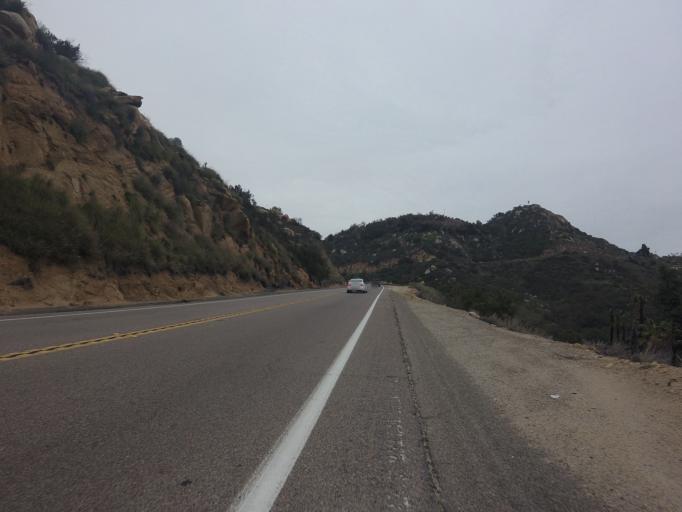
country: US
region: California
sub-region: San Diego County
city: Hidden Meadows
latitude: 33.2532
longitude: -117.1151
